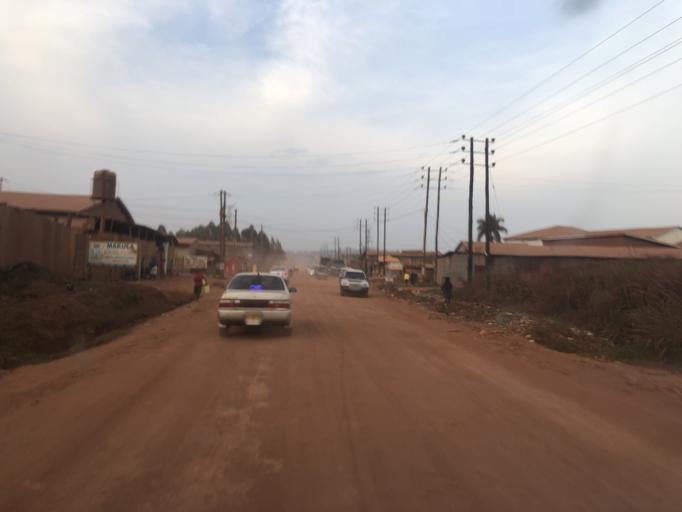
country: UG
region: Central Region
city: Kampala Central Division
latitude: 0.2962
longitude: 32.5234
